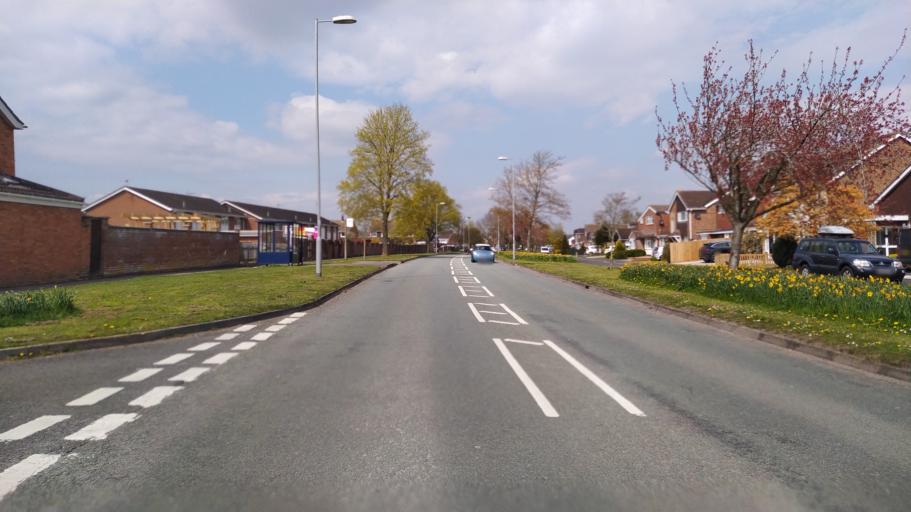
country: GB
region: England
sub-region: Borough of Swindon
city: Wanborough
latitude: 51.5680
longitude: -1.7273
